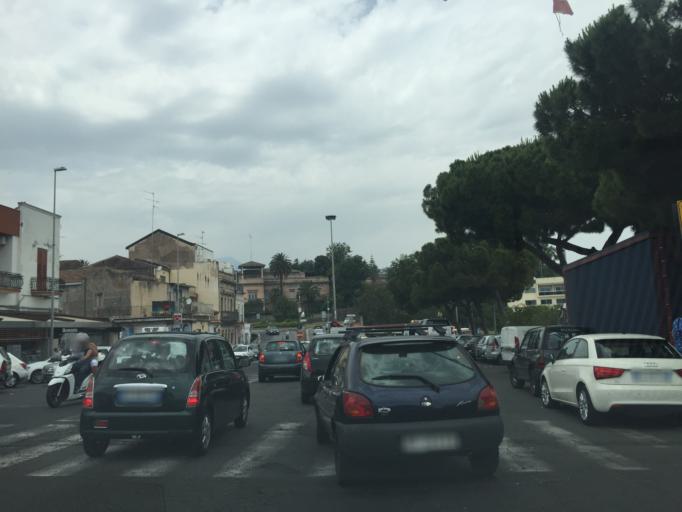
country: IT
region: Sicily
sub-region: Catania
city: Cerza
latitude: 37.5304
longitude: 15.1121
